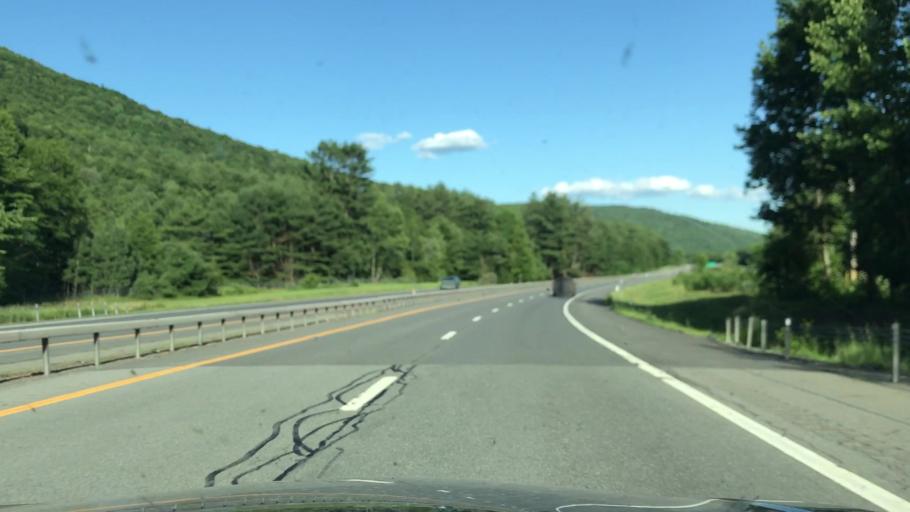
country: US
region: New York
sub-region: Delaware County
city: Hancock
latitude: 41.9868
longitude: -75.1176
